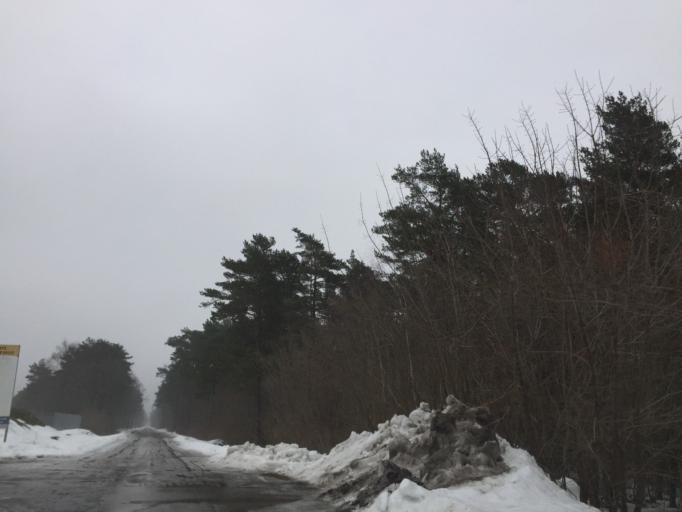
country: EE
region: Saare
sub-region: Kuressaare linn
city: Kuressaare
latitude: 58.2661
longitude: 22.5355
